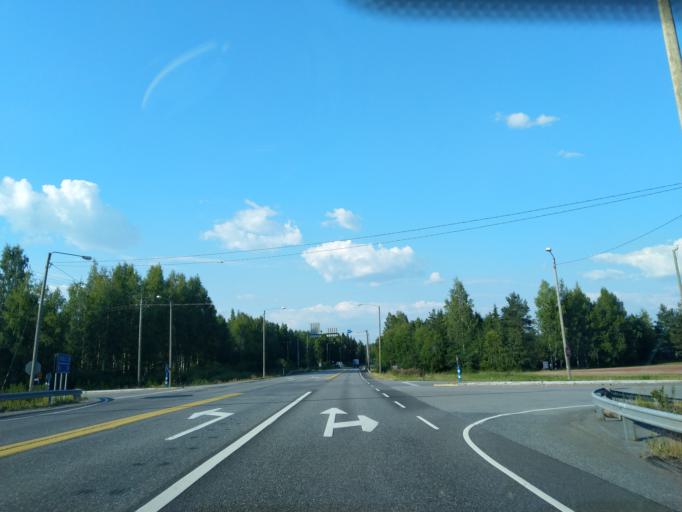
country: FI
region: Satakunta
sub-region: Pori
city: Pomarkku
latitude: 61.6997
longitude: 22.0106
